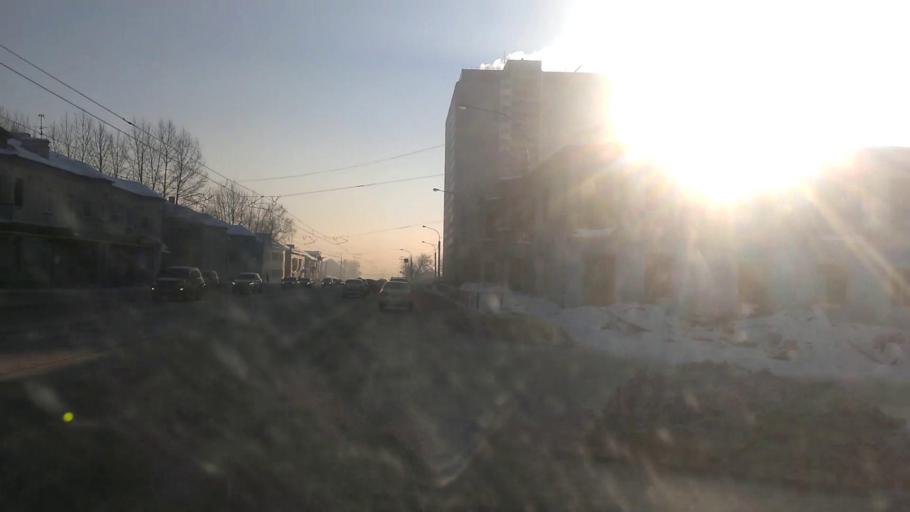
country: RU
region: Altai Krai
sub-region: Gorod Barnaulskiy
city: Barnaul
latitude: 53.3469
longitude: 83.7313
